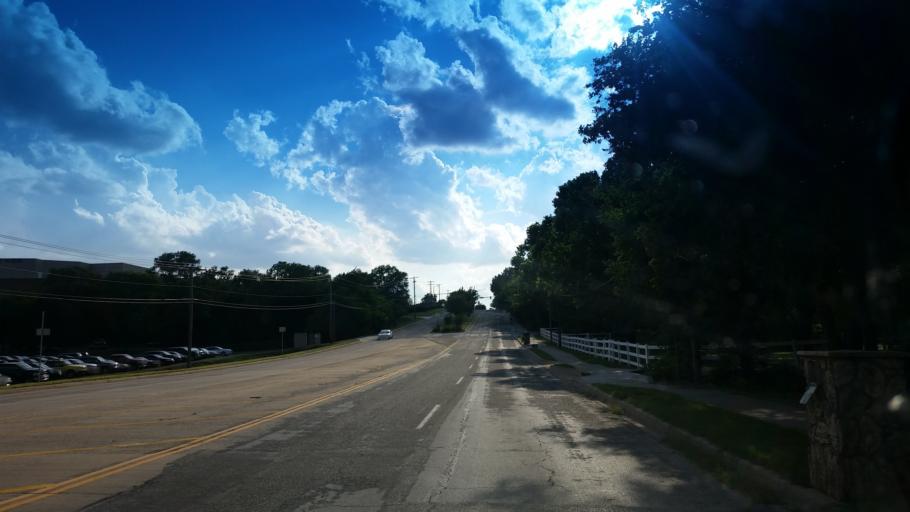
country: US
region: Oklahoma
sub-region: Oklahoma County
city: Nichols Hills
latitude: 35.5368
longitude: -97.4797
